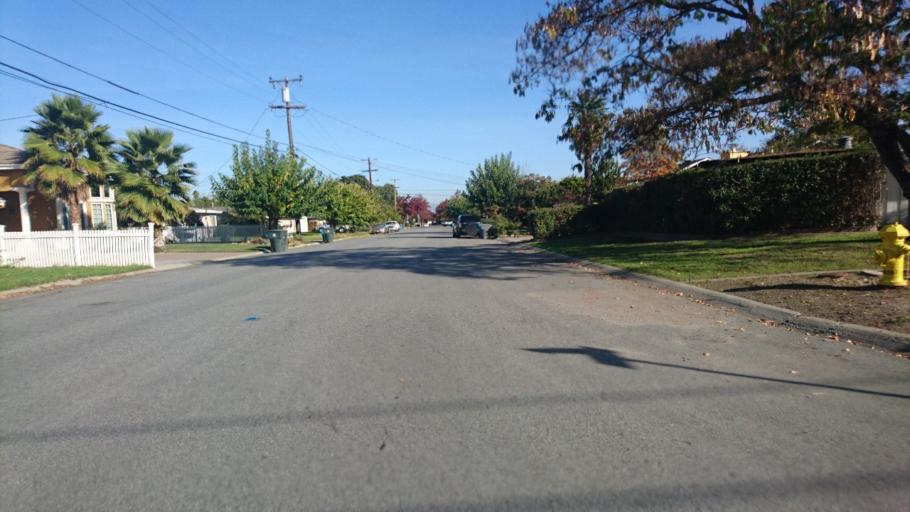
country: US
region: California
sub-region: Santa Clara County
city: Cambrian Park
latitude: 37.2540
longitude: -121.9194
